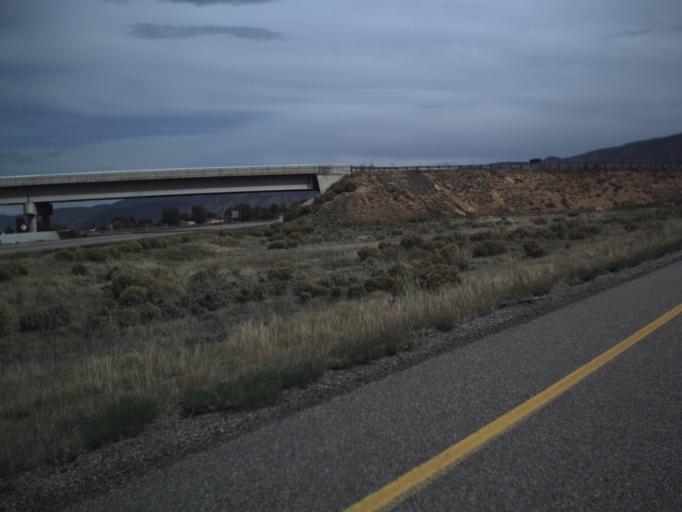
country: US
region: Utah
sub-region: Iron County
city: Parowan
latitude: 37.8382
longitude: -112.8708
